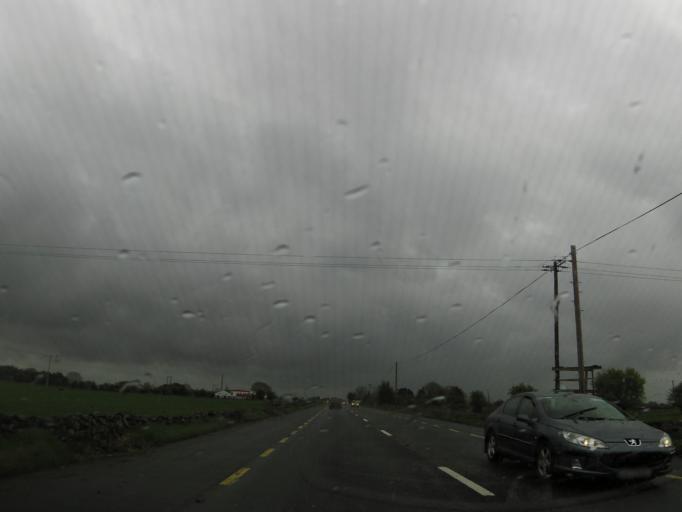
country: IE
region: Connaught
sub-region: County Galway
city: Claregalway
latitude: 53.3687
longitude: -8.9236
